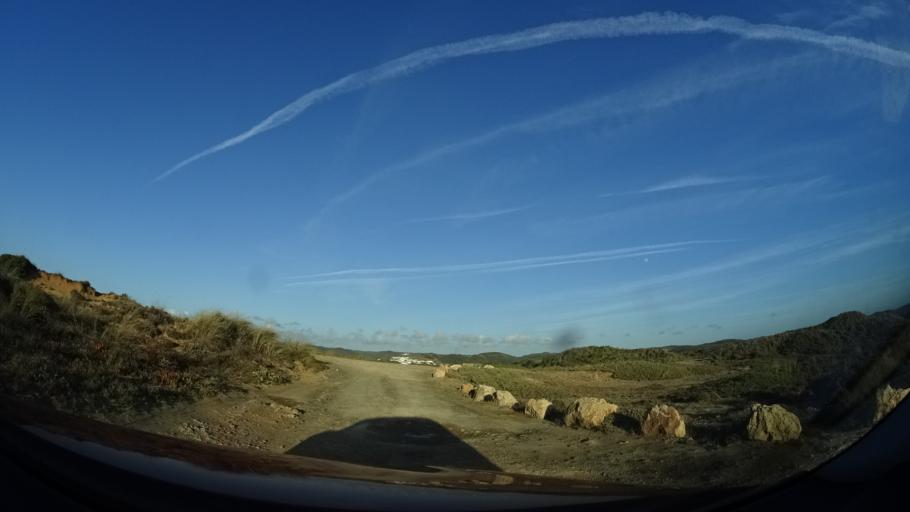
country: PT
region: Faro
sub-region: Vila do Bispo
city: Vila do Bispo
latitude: 37.1833
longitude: -8.9111
